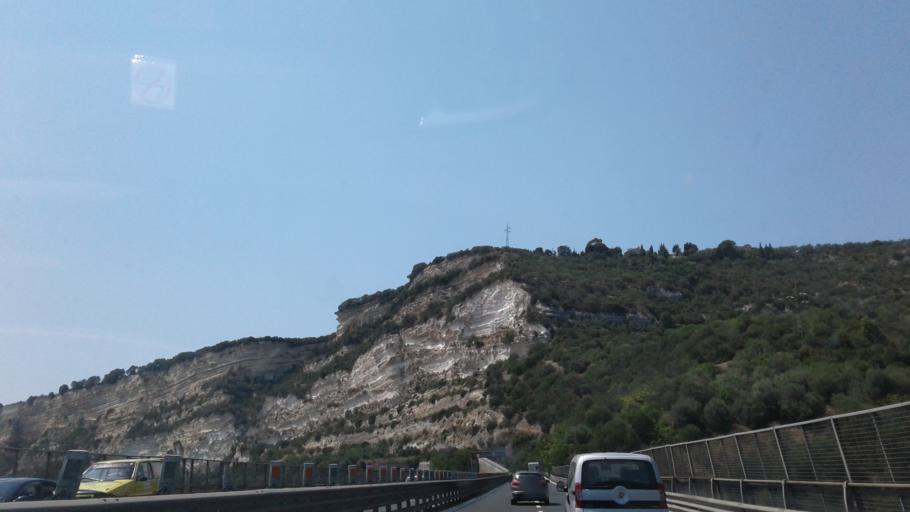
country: IT
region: Sardinia
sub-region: Provincia di Sassari
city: Ossi
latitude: 40.6998
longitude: 8.5921
